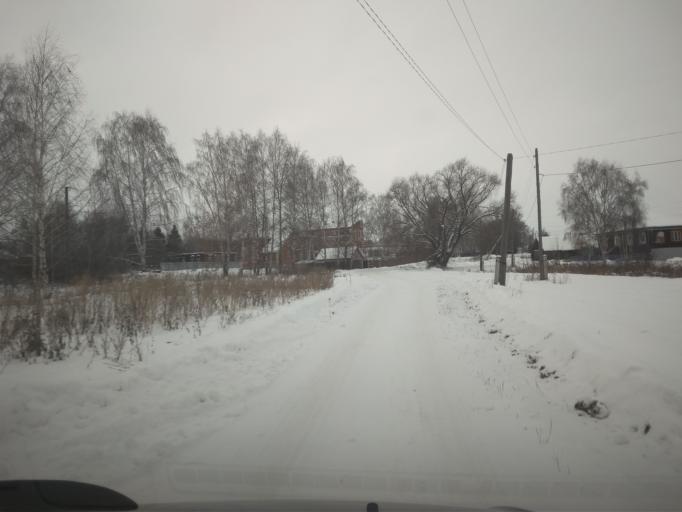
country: RU
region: Mordoviya
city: Ten'gushevo
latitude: 54.7601
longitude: 42.7197
